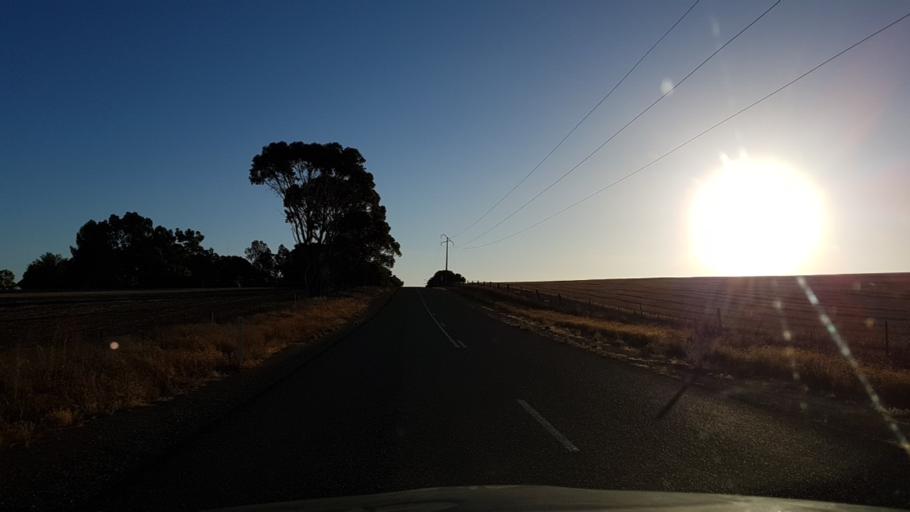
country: AU
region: South Australia
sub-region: Clare and Gilbert Valleys
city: Clare
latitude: -34.0208
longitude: 138.7001
